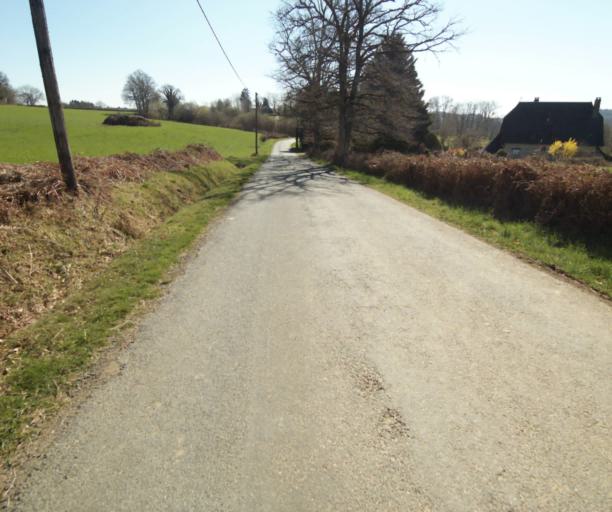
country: FR
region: Limousin
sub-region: Departement de la Correze
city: Saint-Clement
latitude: 45.3380
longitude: 1.6503
